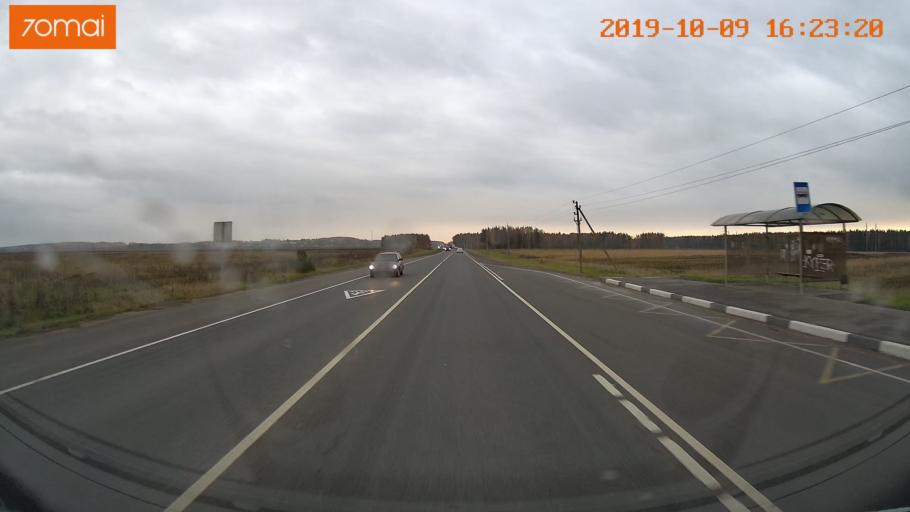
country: RU
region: Kostroma
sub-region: Kostromskoy Rayon
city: Kostroma
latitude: 57.6648
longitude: 40.8990
